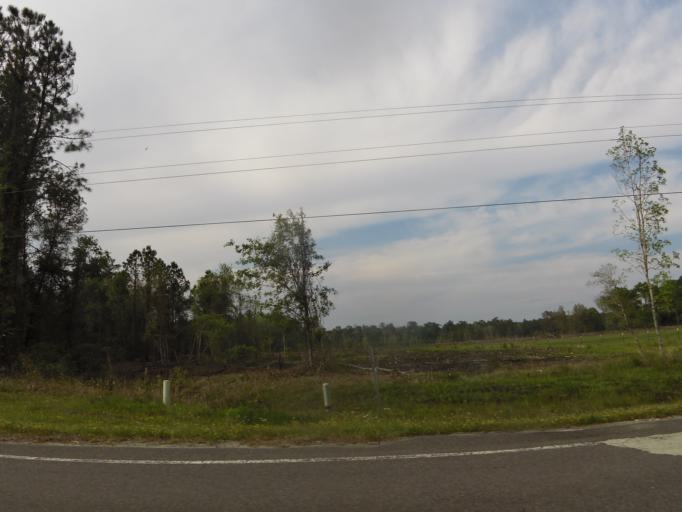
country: US
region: Georgia
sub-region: Camden County
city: Kingsland
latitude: 30.6958
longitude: -81.7387
